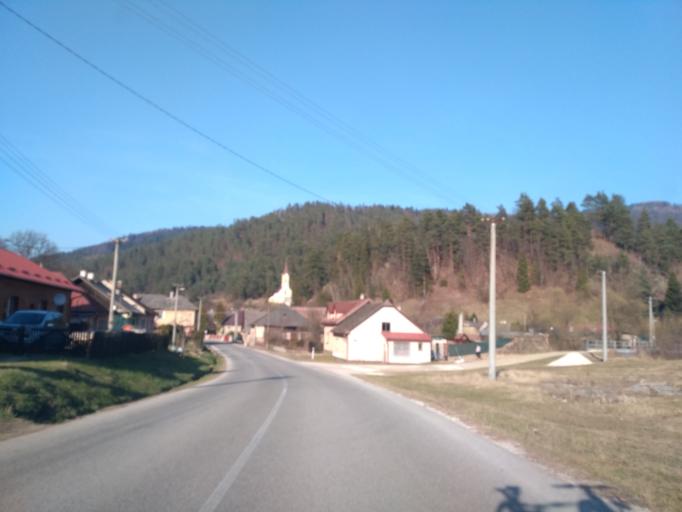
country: SK
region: Kosicky
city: Medzev
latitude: 48.7438
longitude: 20.7721
